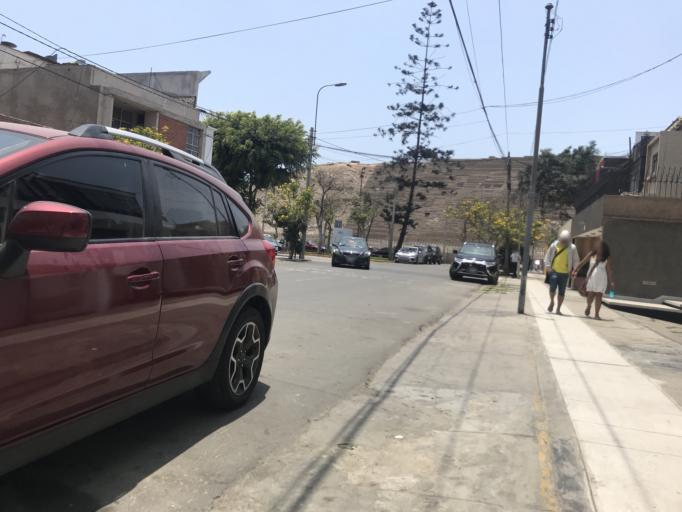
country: PE
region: Lima
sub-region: Lima
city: San Isidro
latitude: -12.1115
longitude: -77.0327
